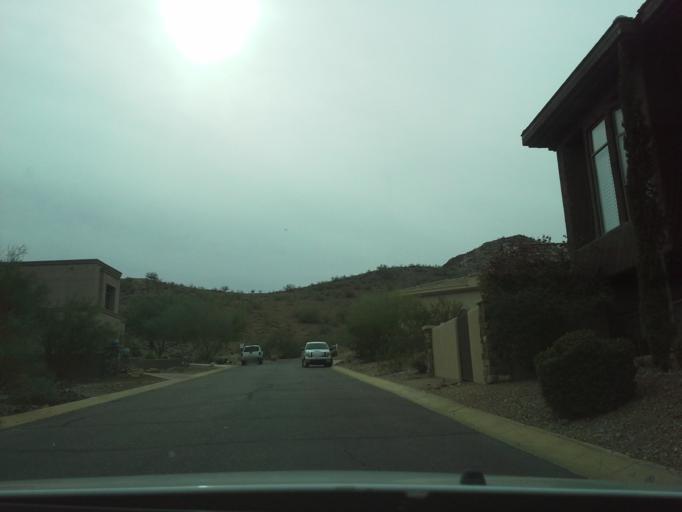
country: US
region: Arizona
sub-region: Maricopa County
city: Paradise Valley
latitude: 33.6178
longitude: -112.0253
